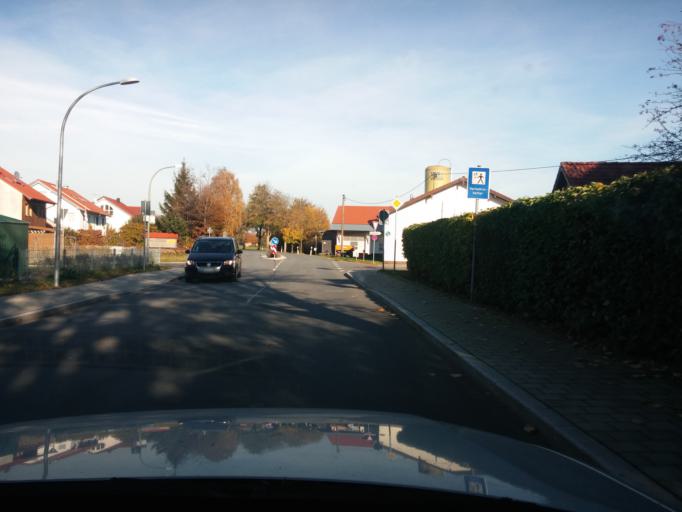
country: DE
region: Bavaria
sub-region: Upper Bavaria
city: Pastetten
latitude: 48.2016
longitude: 11.9497
